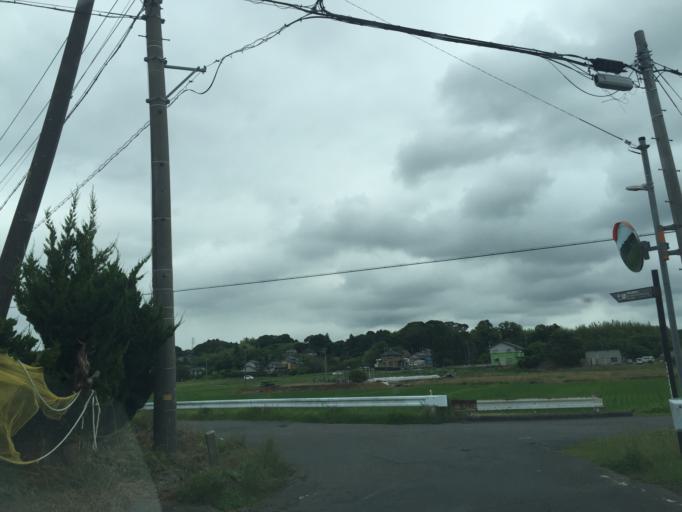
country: JP
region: Shizuoka
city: Fukuroi
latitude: 34.7687
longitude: 137.9307
